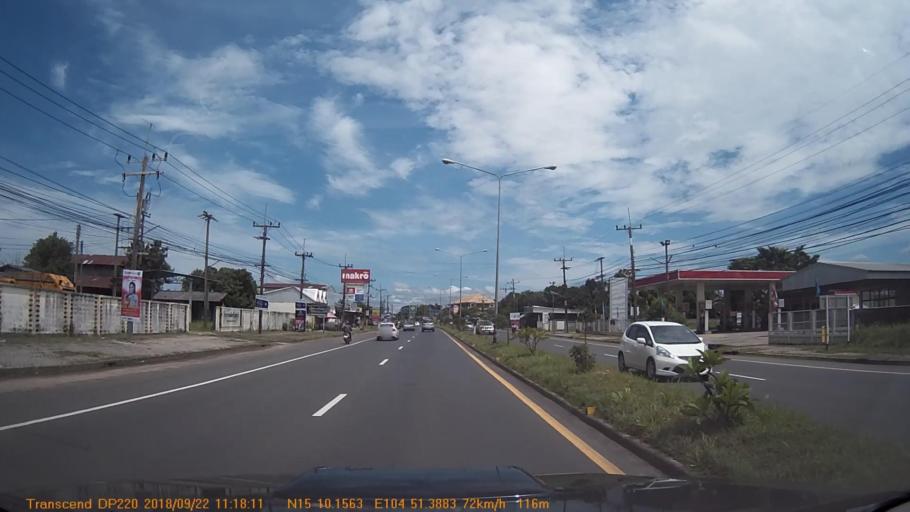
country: TH
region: Changwat Ubon Ratchathani
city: Warin Chamrap
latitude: 15.1693
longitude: 104.8565
